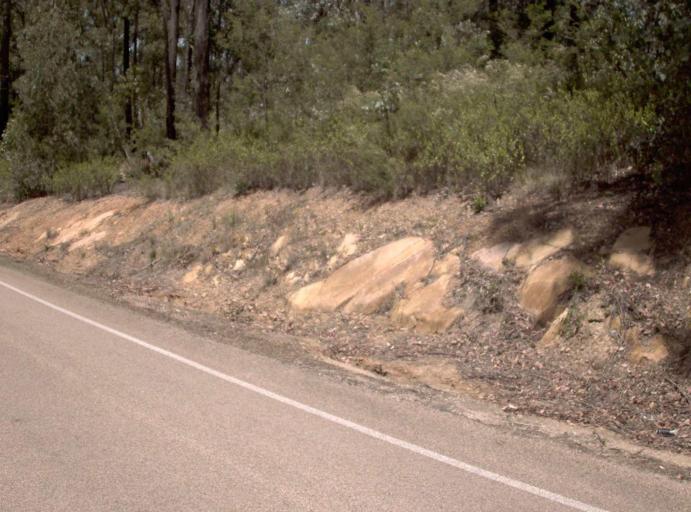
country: AU
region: Victoria
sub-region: East Gippsland
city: Lakes Entrance
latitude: -37.6248
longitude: 147.8838
